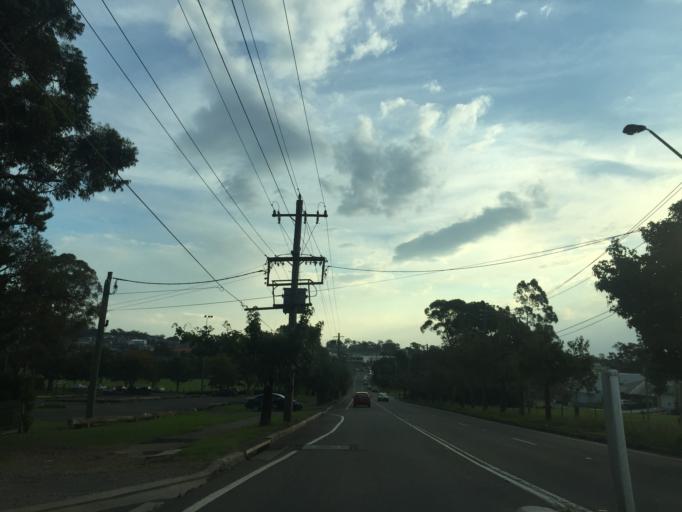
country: AU
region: New South Wales
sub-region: The Hills Shire
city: Beaumont Hills
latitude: -33.7165
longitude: 150.9588
